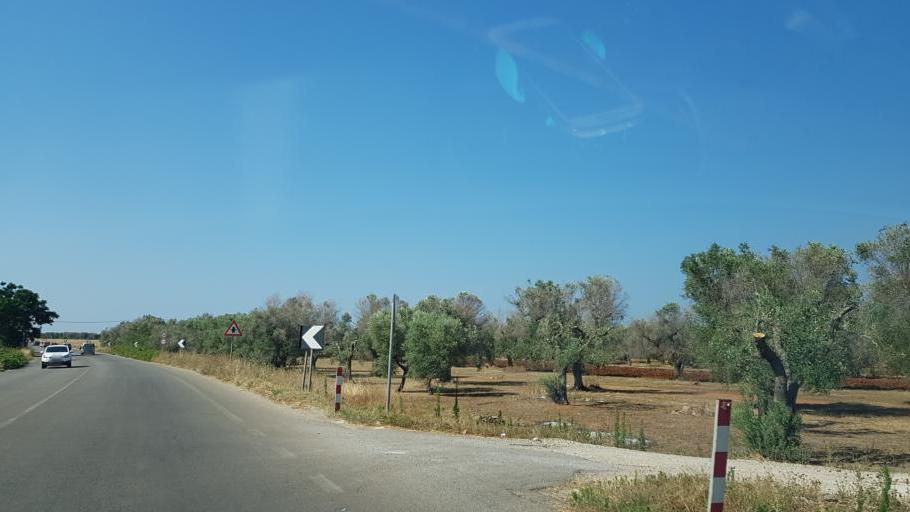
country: IT
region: Apulia
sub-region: Provincia di Lecce
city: Veglie
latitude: 40.3401
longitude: 17.9417
